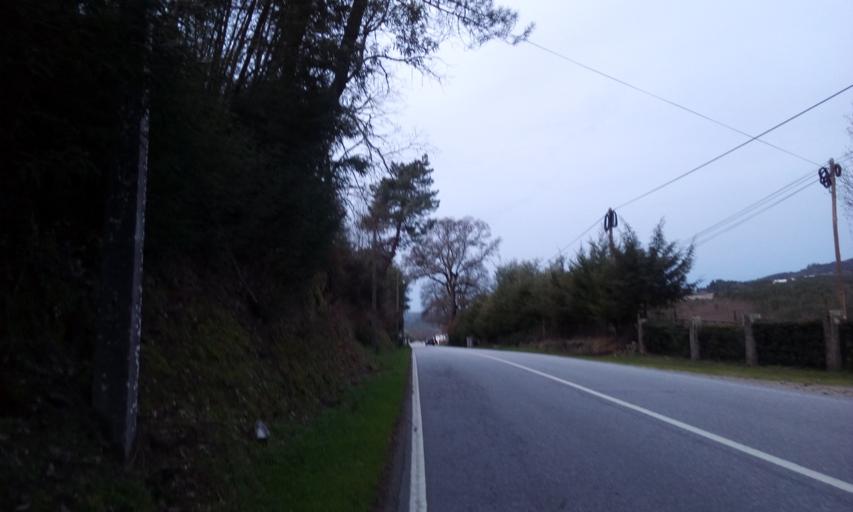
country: PT
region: Guarda
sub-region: Fornos de Algodres
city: Fornos de Algodres
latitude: 40.6143
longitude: -7.5125
